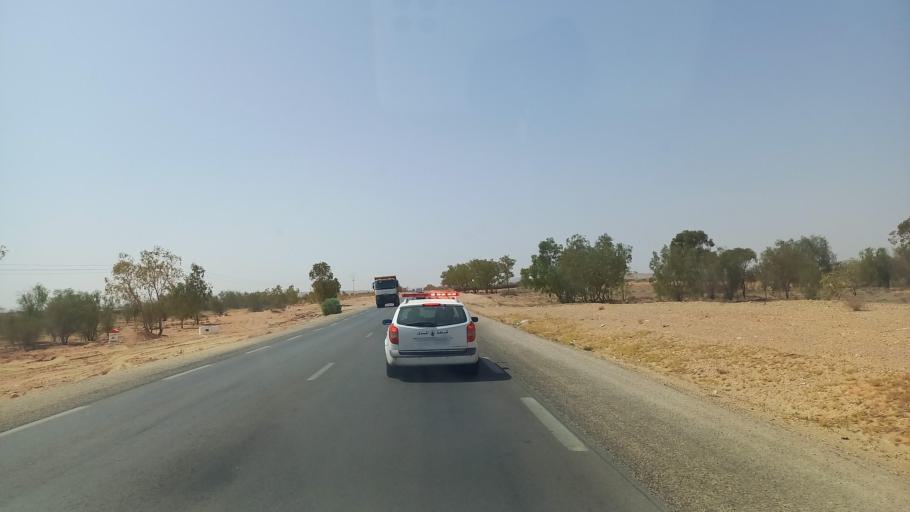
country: TN
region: Madanin
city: Medenine
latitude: 33.2231
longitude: 10.4505
